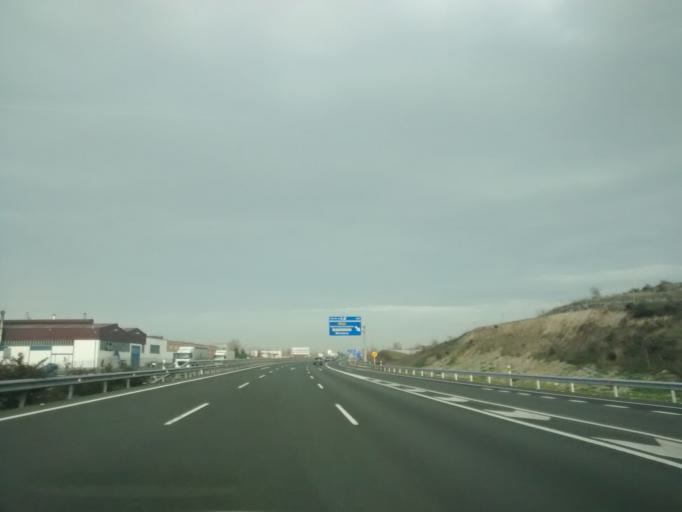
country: ES
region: Basque Country
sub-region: Provincia de Alava
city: Arminon
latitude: 42.8122
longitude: -2.7945
